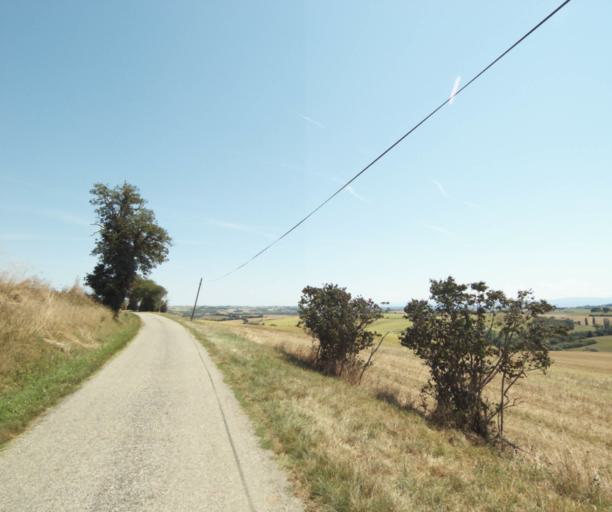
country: FR
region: Midi-Pyrenees
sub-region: Departement de l'Ariege
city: Lezat-sur-Leze
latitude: 43.2771
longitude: 1.3135
